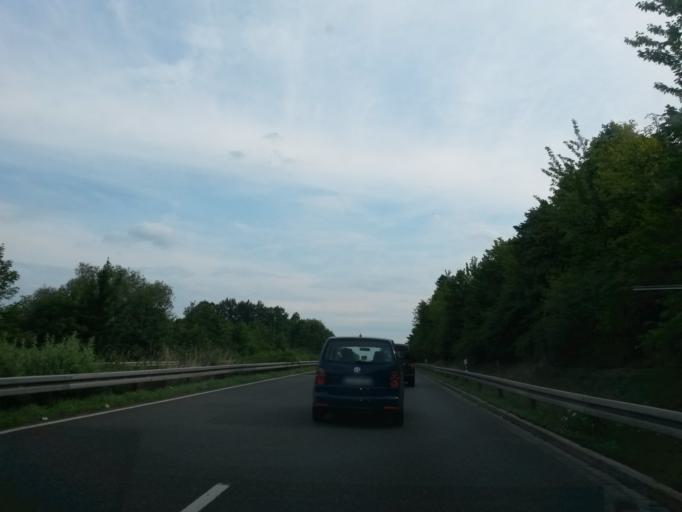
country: DE
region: Bavaria
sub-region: Regierungsbezirk Mittelfranken
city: Zirndorf
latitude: 49.4505
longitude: 10.9753
